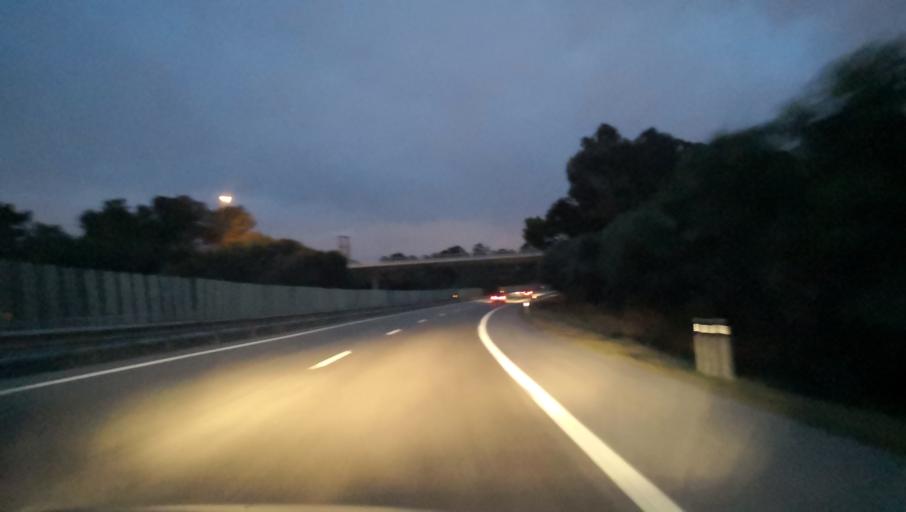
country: PT
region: Setubal
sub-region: Barreiro
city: Santo Antonio da Charneca
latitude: 38.6309
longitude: -9.0421
